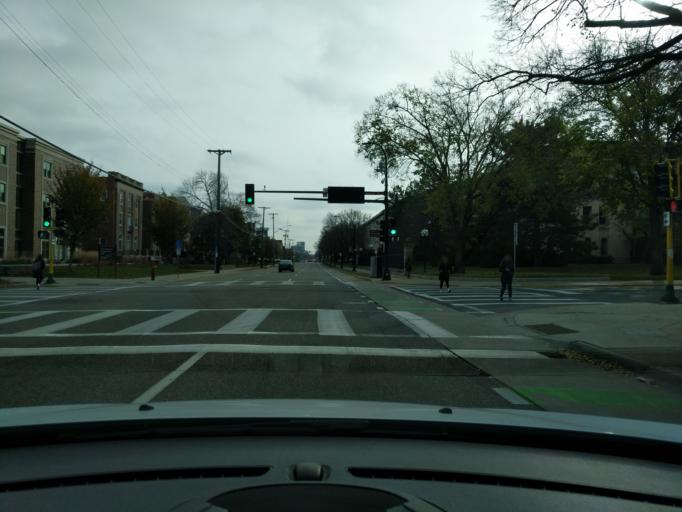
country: US
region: Minnesota
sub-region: Hennepin County
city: Minneapolis
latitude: 44.9780
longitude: -93.2327
